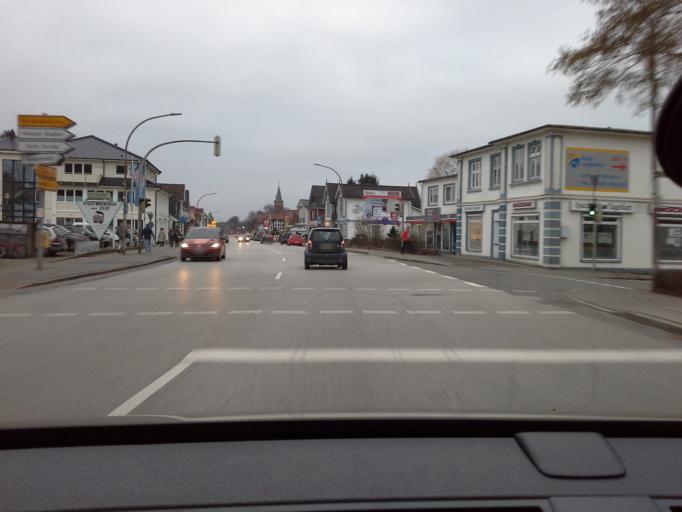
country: DE
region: Schleswig-Holstein
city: Quickborn
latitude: 53.7286
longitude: 9.8982
